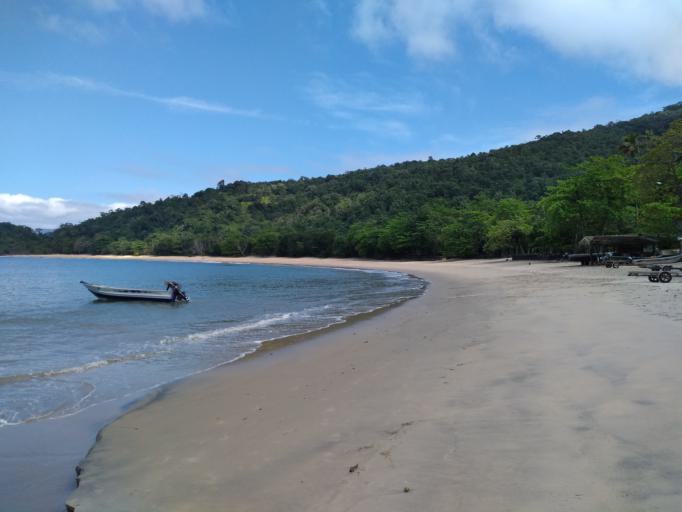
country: BR
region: Sao Paulo
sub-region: Ubatuba
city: Ubatuba
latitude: -23.5384
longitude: -45.1770
